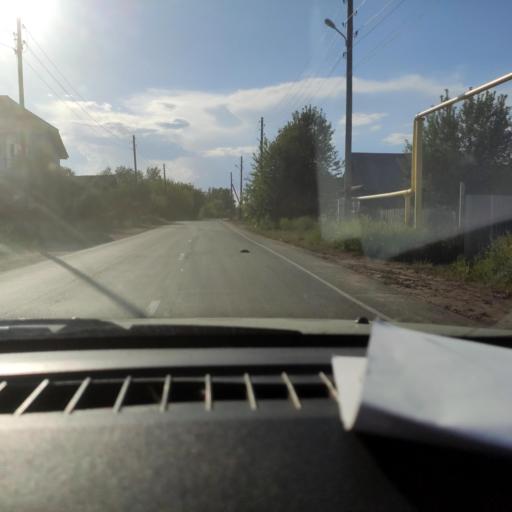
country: RU
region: Perm
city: Krasnokamsk
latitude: 58.1424
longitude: 55.7344
